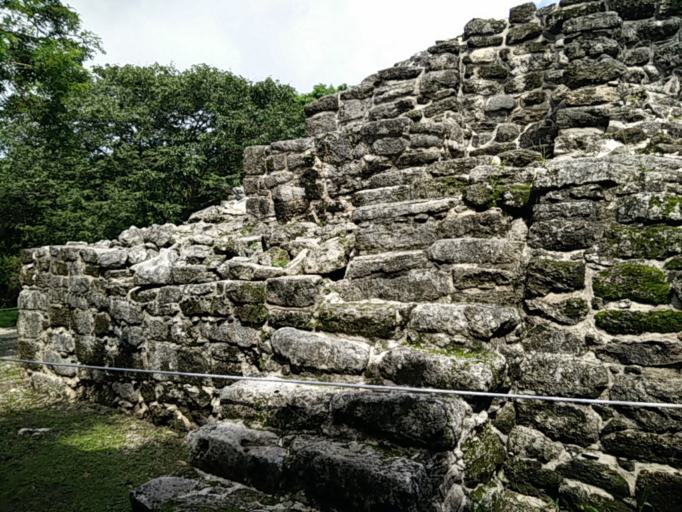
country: MX
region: Quintana Roo
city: San Miguel de Cozumel
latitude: 20.5020
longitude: -86.8517
